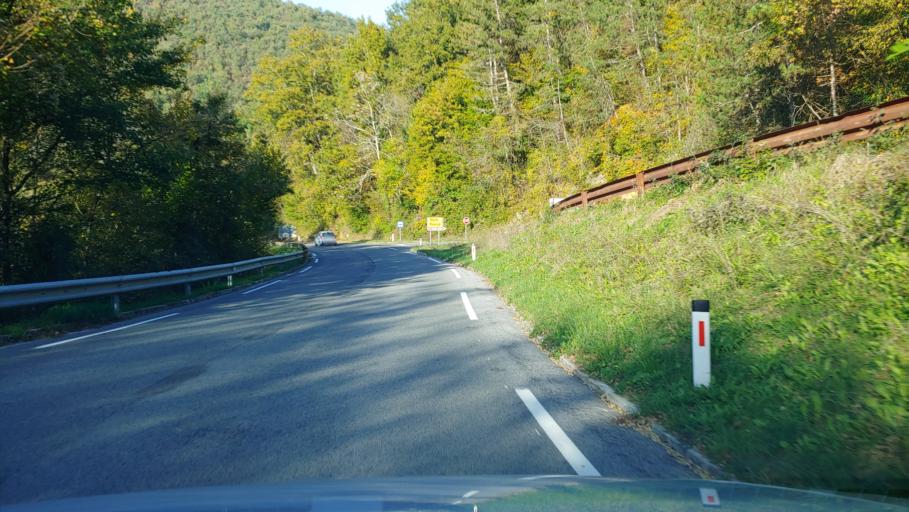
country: SI
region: Ajdovscina
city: Ajdovscina
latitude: 45.8050
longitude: 13.8657
